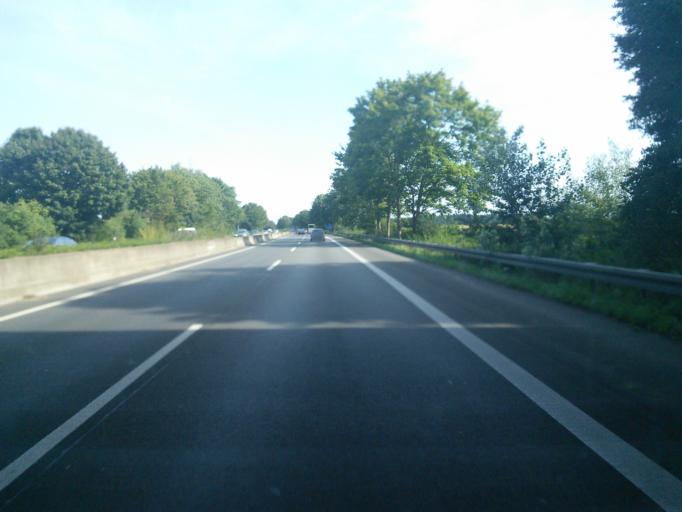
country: DE
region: North Rhine-Westphalia
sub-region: Regierungsbezirk Koln
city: Sinnersdorf
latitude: 51.0318
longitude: 6.8427
